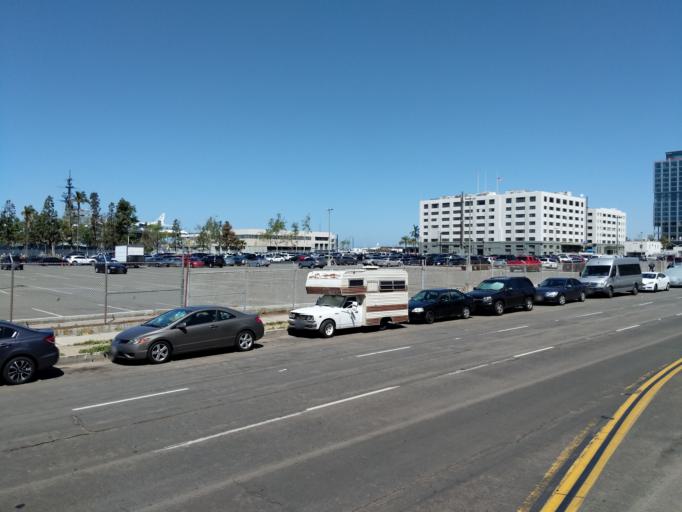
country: US
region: California
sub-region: San Diego County
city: San Diego
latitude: 32.7128
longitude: -117.1710
